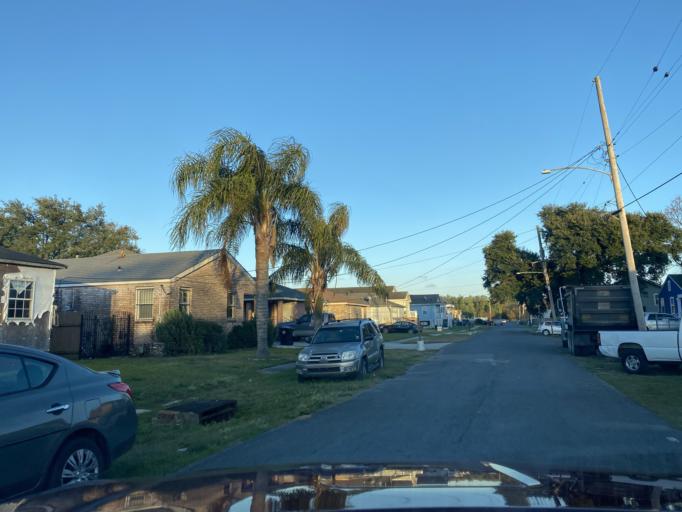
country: US
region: Louisiana
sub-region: Orleans Parish
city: New Orleans
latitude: 30.0259
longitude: -90.0509
